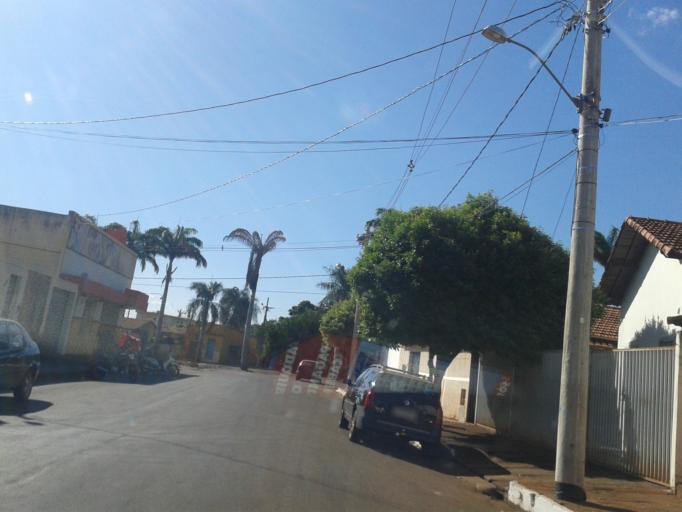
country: BR
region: Minas Gerais
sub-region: Capinopolis
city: Capinopolis
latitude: -18.6887
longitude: -49.5689
